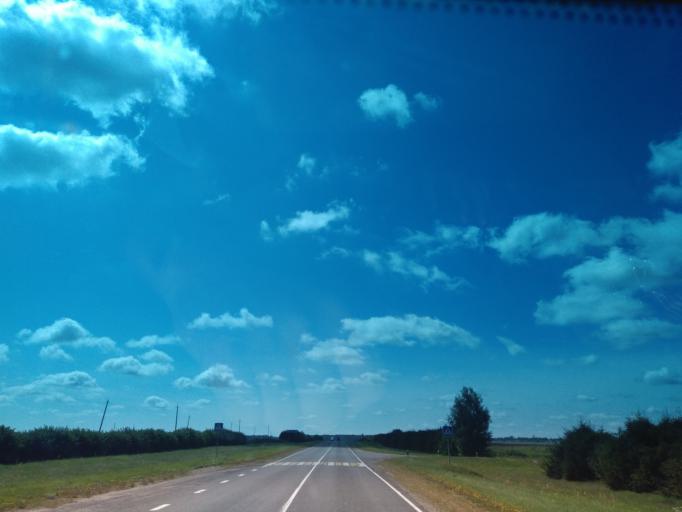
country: BY
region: Minsk
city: Uzda
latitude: 53.3764
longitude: 27.2367
